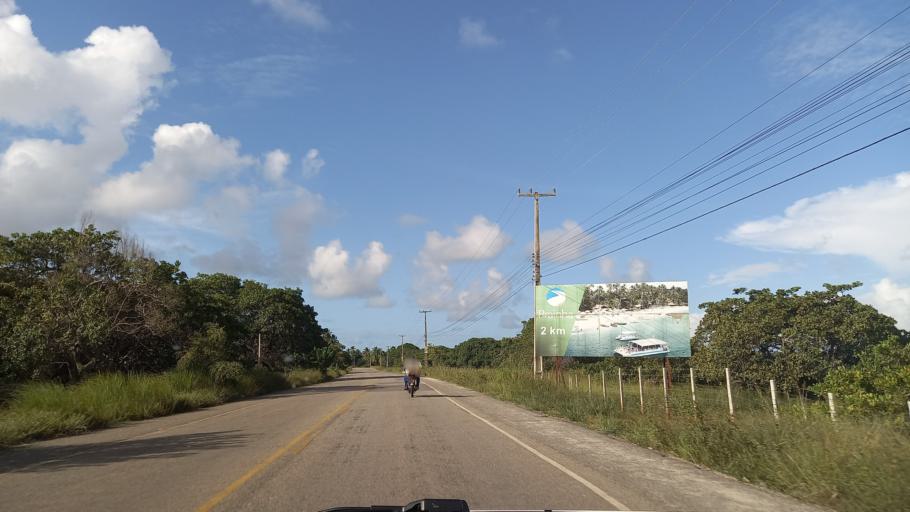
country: BR
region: Pernambuco
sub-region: Tamandare
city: Tamandare
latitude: -8.7139
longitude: -35.0922
